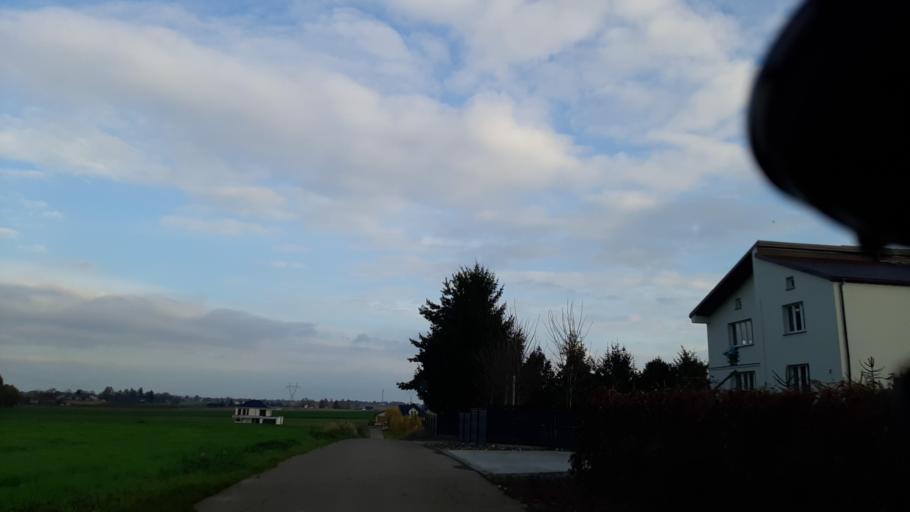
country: PL
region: Lublin Voivodeship
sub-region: Powiat lubelski
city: Garbow
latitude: 51.3383
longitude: 22.3207
